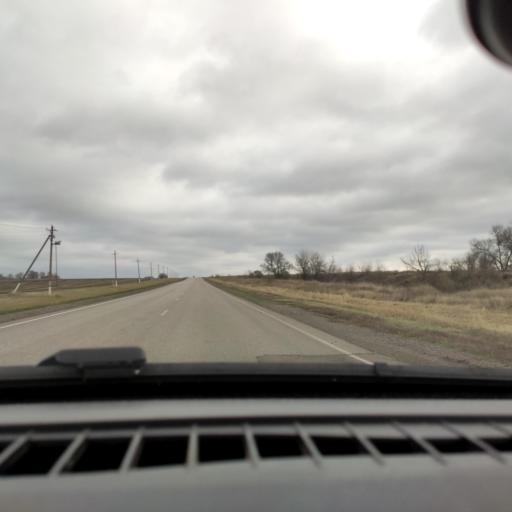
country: RU
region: Belgorod
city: Ilovka
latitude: 50.7688
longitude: 38.7575
